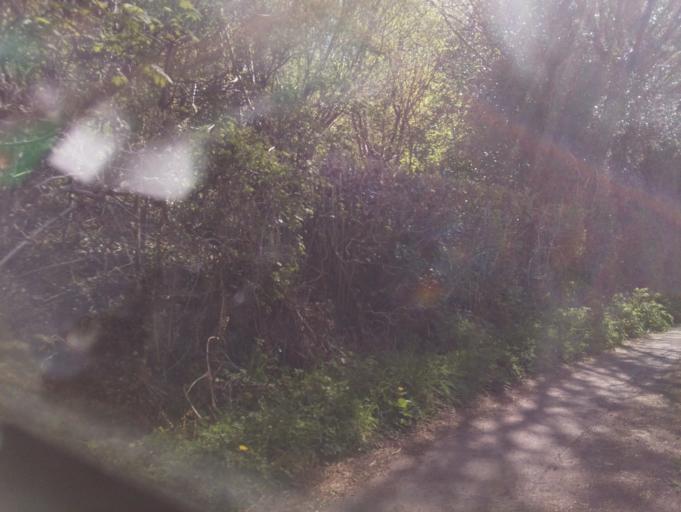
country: GB
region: Wales
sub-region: Monmouthshire
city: Llangwm
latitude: 51.6841
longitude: -2.8119
